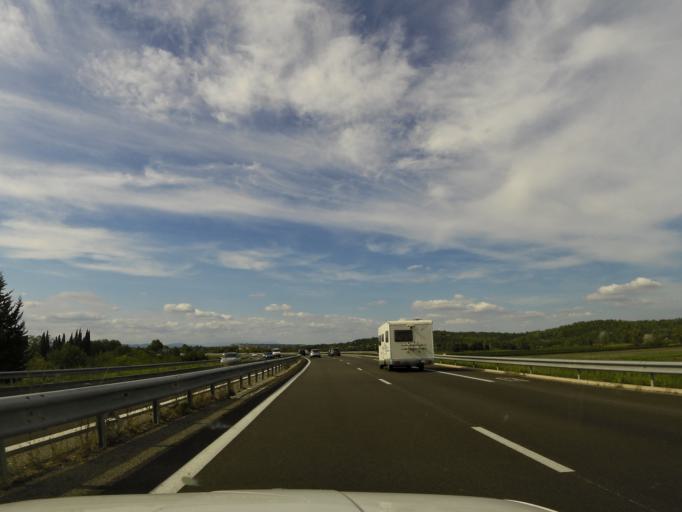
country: FR
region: Languedoc-Roussillon
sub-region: Departement du Gard
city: Vezenobres
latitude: 44.0073
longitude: 4.1747
